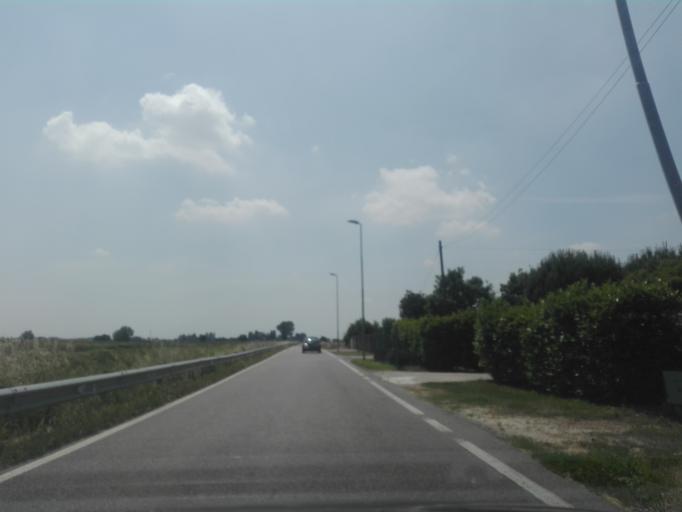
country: IT
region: Veneto
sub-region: Provincia di Rovigo
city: Grignano Polesine
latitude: 45.0411
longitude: 11.7353
